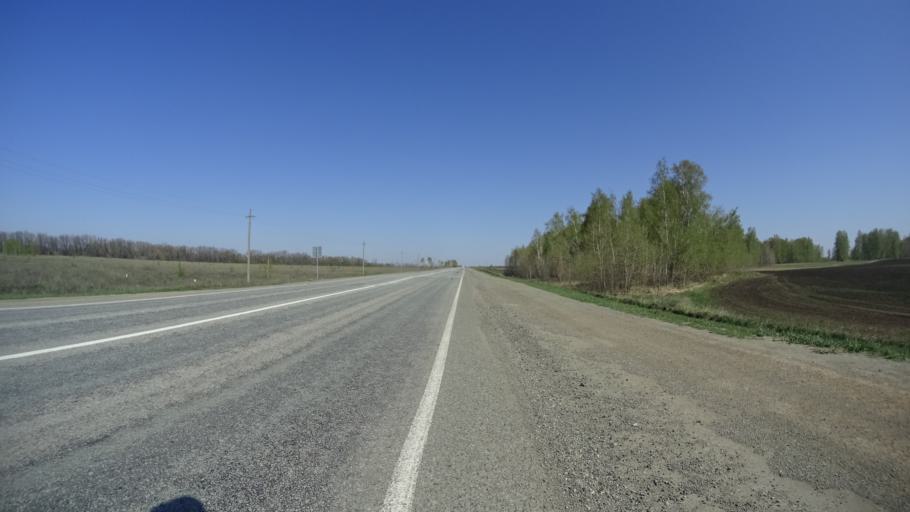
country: RU
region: Chelyabinsk
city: Troitsk
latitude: 54.1895
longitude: 61.4337
